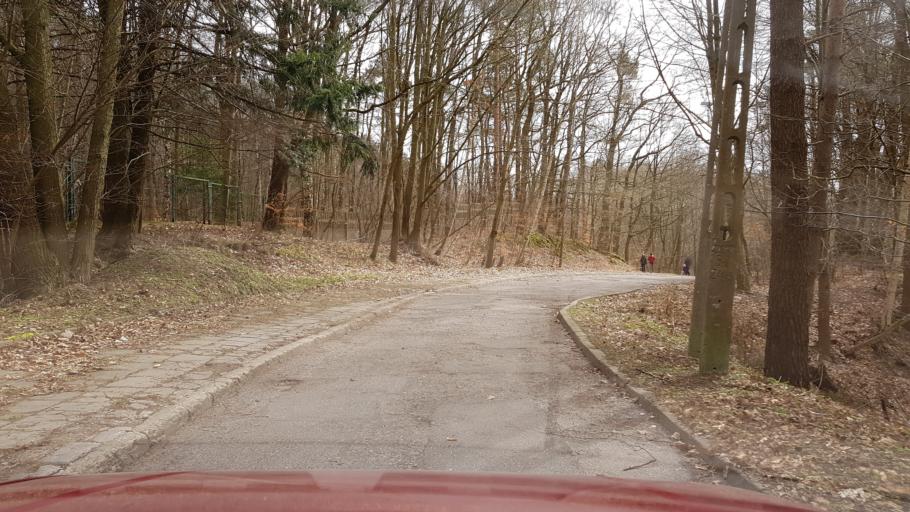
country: PL
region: West Pomeranian Voivodeship
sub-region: Koszalin
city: Koszalin
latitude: 54.1980
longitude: 16.2289
